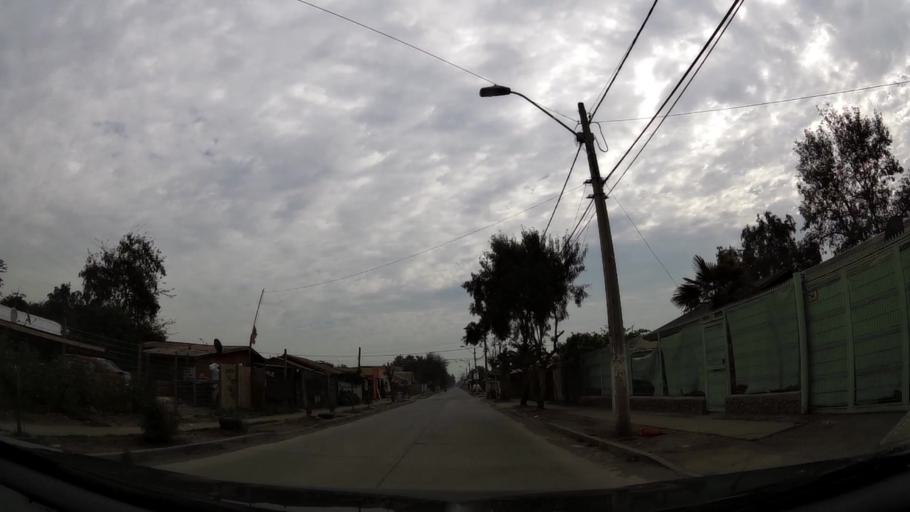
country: CL
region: Santiago Metropolitan
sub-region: Provincia de Chacabuco
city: Lampa
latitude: -33.2335
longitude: -70.8124
